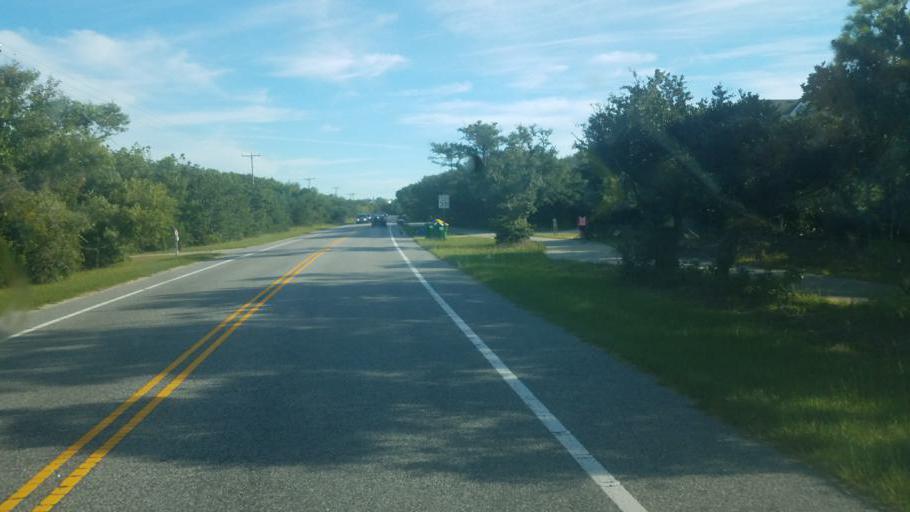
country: US
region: North Carolina
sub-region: Dare County
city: Southern Shores
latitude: 36.2941
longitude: -75.8026
